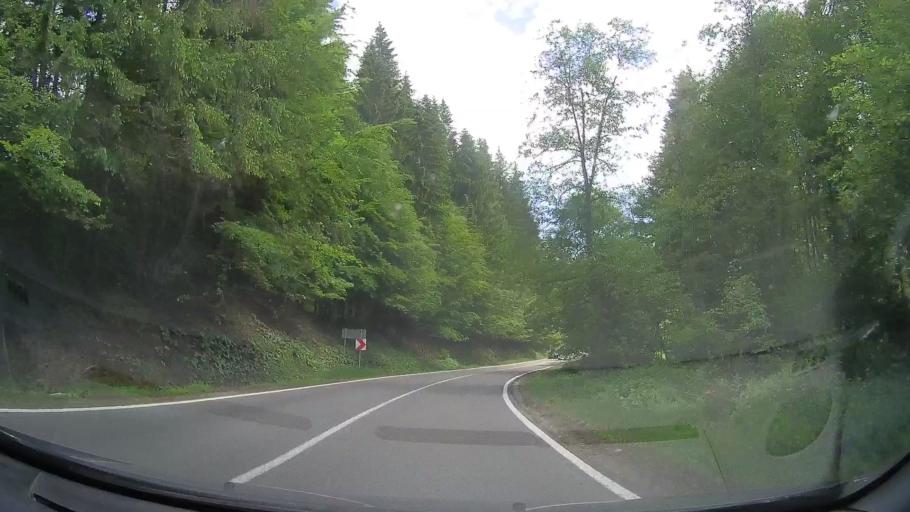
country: RO
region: Brasov
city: Crivina
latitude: 45.4574
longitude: 25.9509
